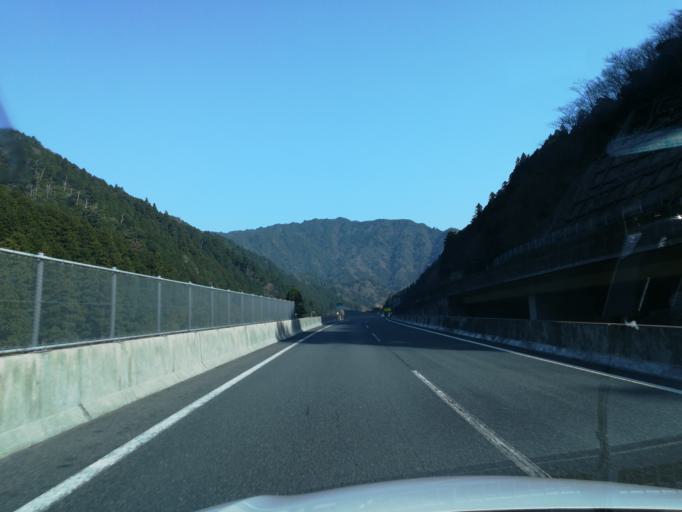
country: JP
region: Ehime
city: Kawanoecho
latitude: 33.9011
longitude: 133.6316
